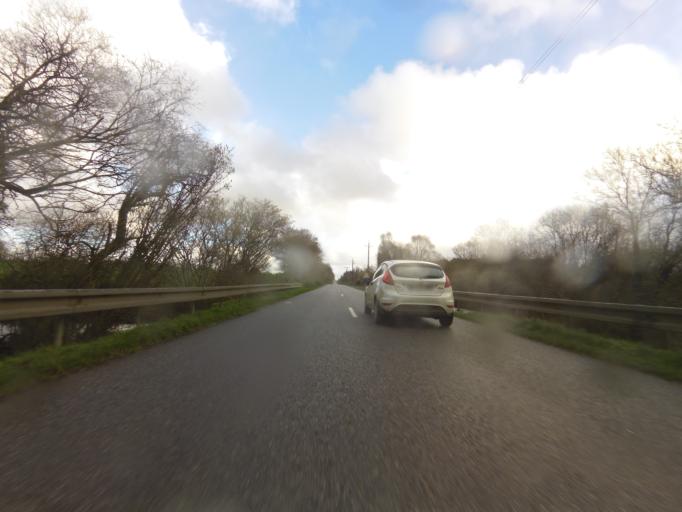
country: FR
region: Brittany
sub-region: Departement du Morbihan
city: Langonnet
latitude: 48.1440
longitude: -3.4803
